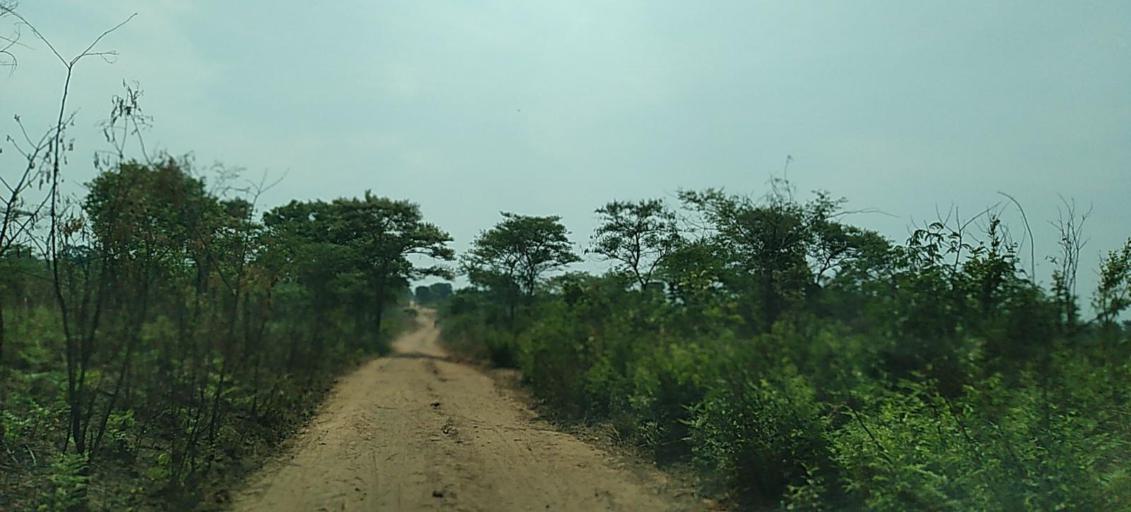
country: ZM
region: Copperbelt
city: Ndola
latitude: -13.2096
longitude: 28.7359
